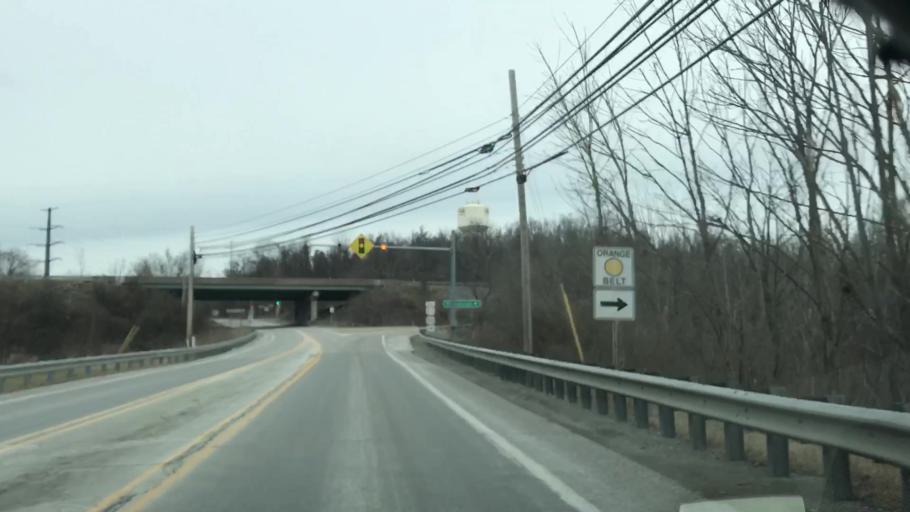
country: US
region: Pennsylvania
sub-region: Allegheny County
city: Oakdale
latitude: 40.4372
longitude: -80.1909
